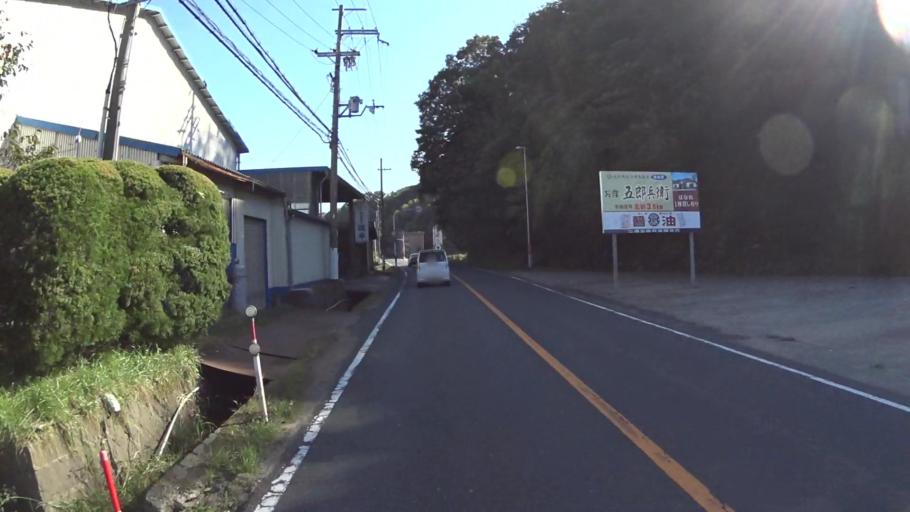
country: JP
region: Kyoto
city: Miyazu
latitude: 35.6667
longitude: 135.0280
